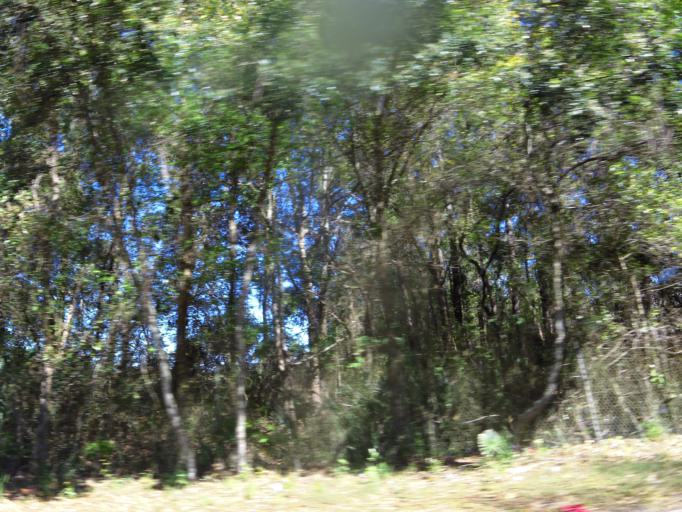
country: US
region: Florida
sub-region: Duval County
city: Jacksonville
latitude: 30.3636
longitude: -81.6434
